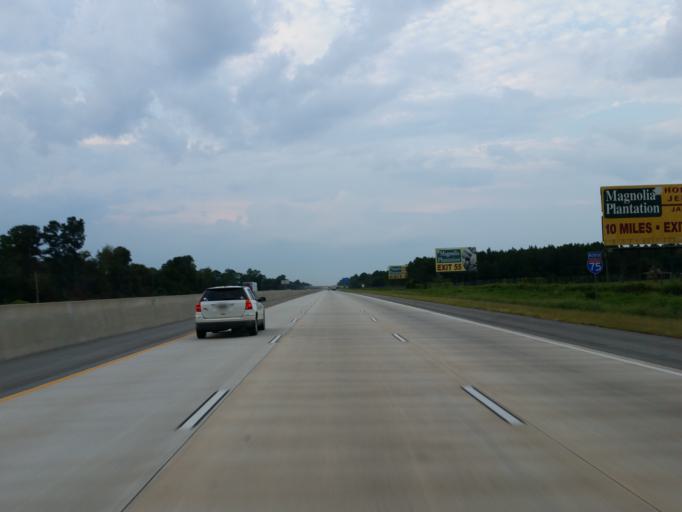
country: US
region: Georgia
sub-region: Cook County
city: Sparks
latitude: 31.2212
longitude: -83.4611
